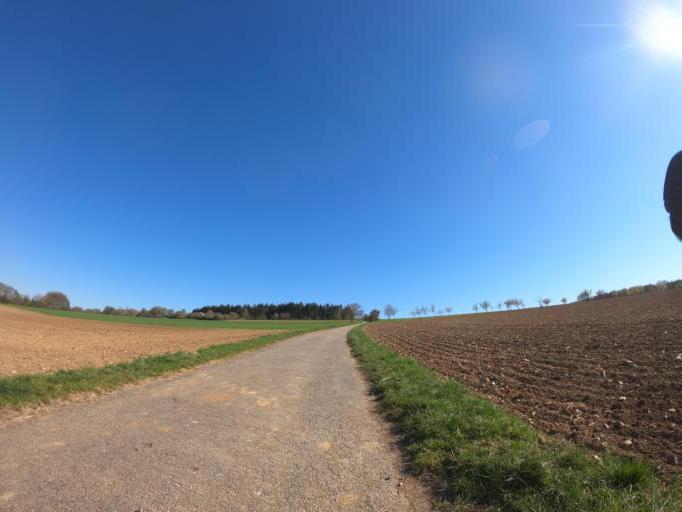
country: DE
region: Baden-Wuerttemberg
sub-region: Karlsruhe Region
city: Wiernsheim
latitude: 48.8846
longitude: 8.8584
